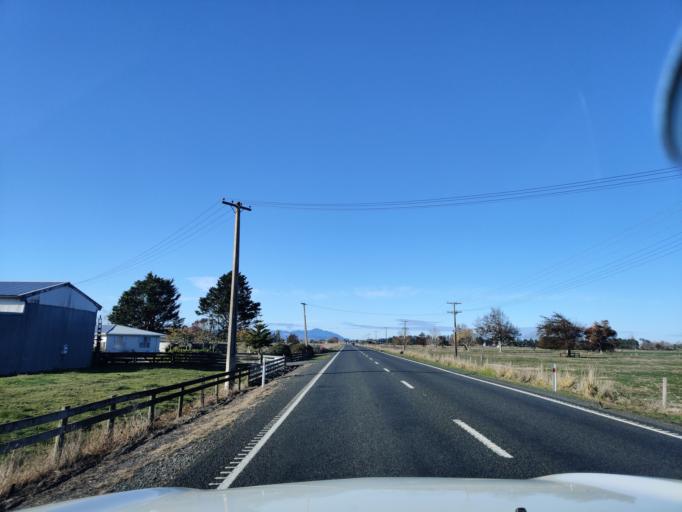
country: NZ
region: Waikato
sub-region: Hauraki District
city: Ngatea
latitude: -37.2881
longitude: 175.5481
